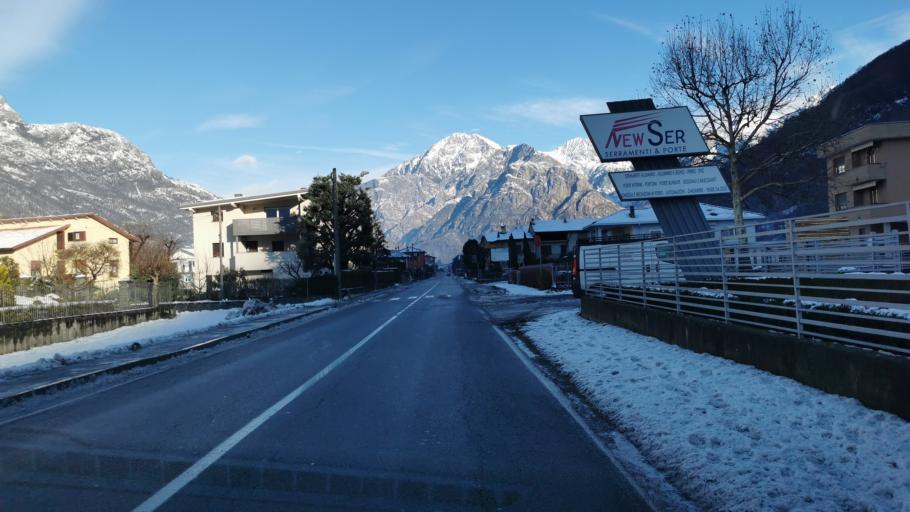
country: IT
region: Lombardy
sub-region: Provincia di Sondrio
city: Dubino
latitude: 46.1637
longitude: 9.4313
